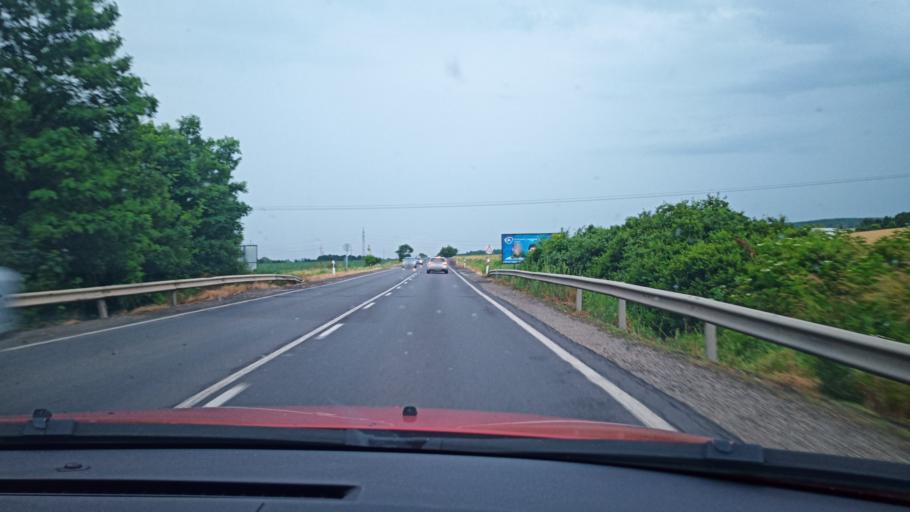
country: HU
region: Borsod-Abauj-Zemplen
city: Malyi
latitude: 48.0479
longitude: 20.8009
